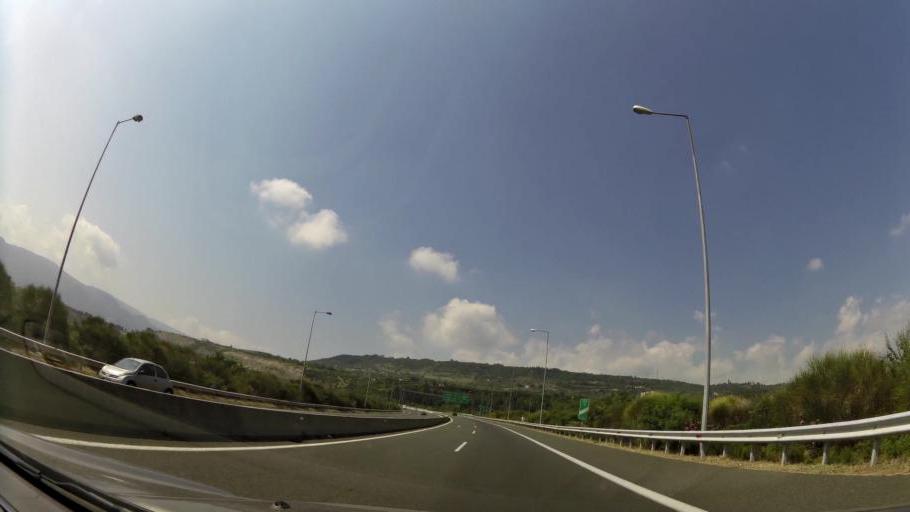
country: GR
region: Central Macedonia
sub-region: Nomos Imathias
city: Veroia
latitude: 40.5103
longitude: 22.2315
